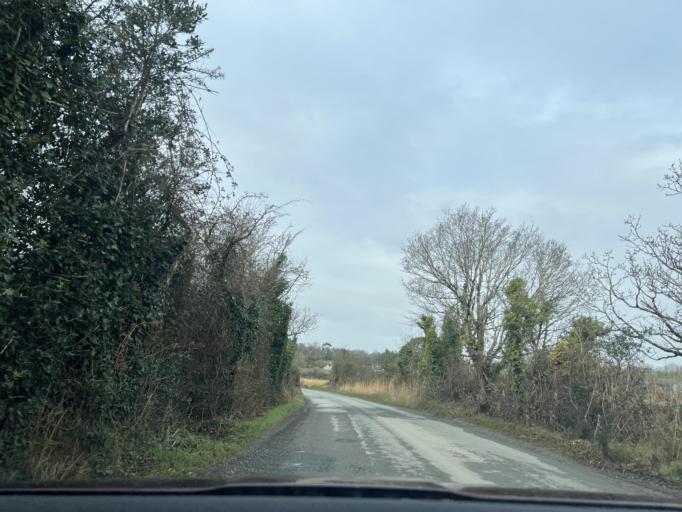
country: IE
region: Leinster
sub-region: Loch Garman
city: Castlebridge
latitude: 52.3844
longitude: -6.5652
